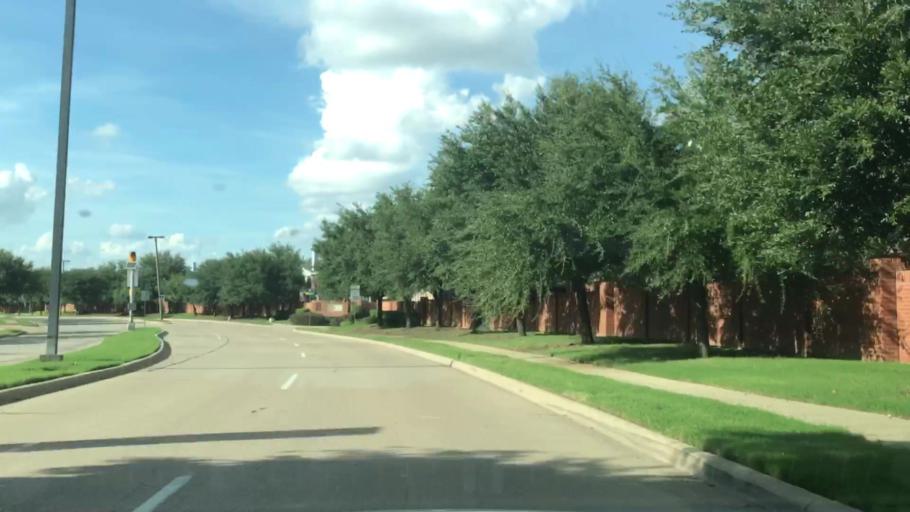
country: US
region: Texas
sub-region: Dallas County
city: Farmers Branch
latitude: 32.9278
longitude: -96.9580
